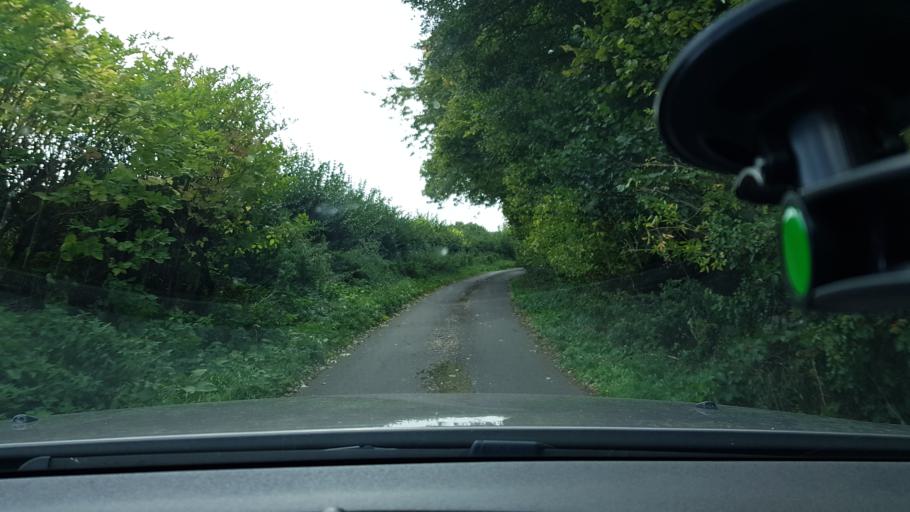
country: GB
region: England
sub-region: West Berkshire
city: Hungerford
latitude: 51.4568
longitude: -1.5000
